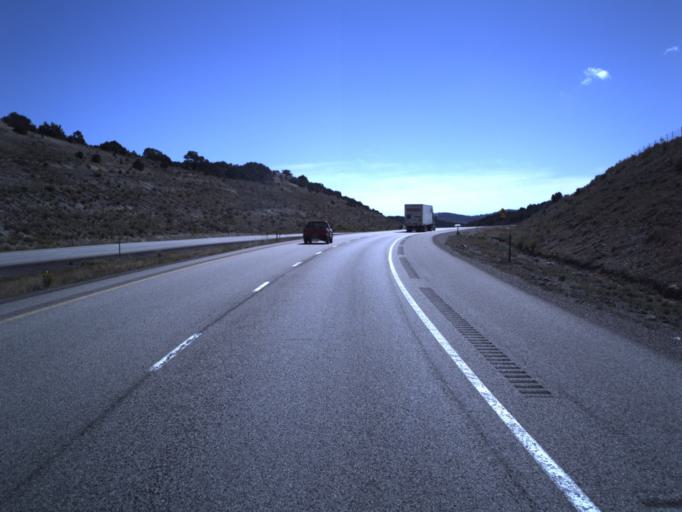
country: US
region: Utah
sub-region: Wayne County
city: Loa
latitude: 38.7822
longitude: -111.4879
